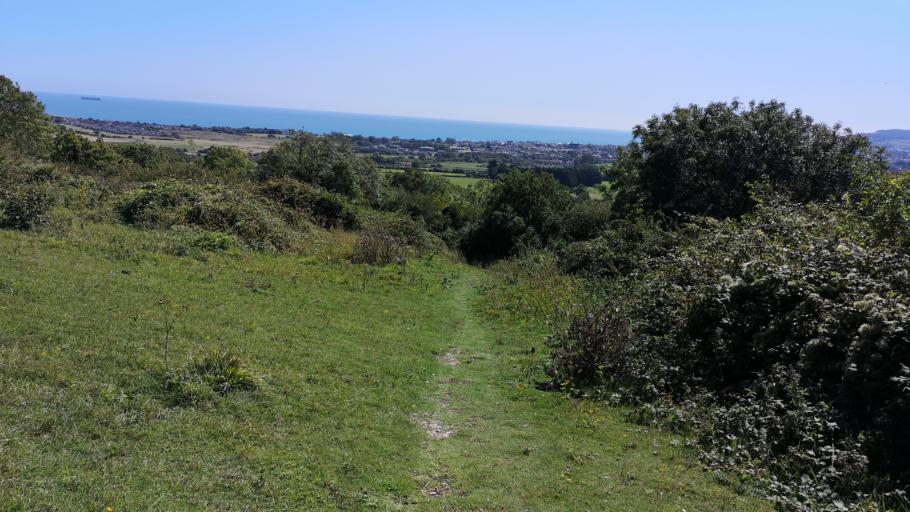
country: GB
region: England
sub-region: Isle of Wight
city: Brading
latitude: 50.6781
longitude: -1.1573
